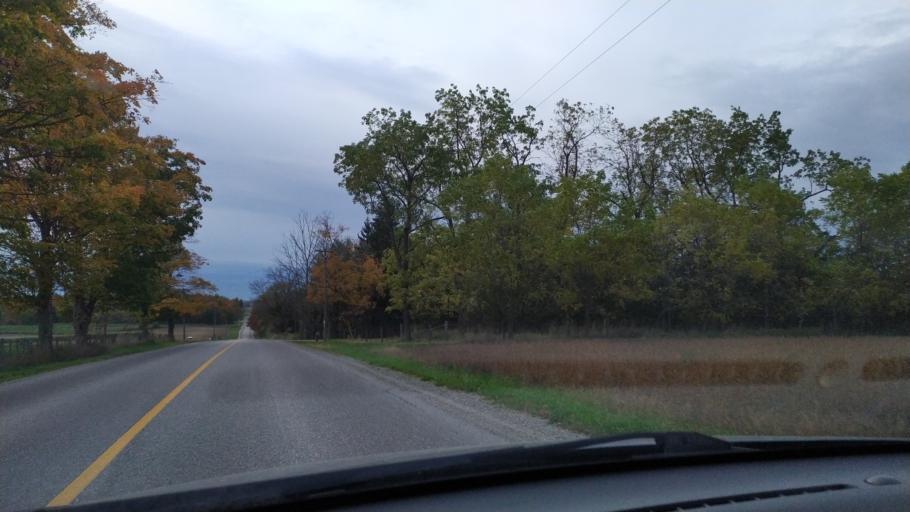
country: CA
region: Ontario
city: Waterloo
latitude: 43.5085
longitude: -80.6990
